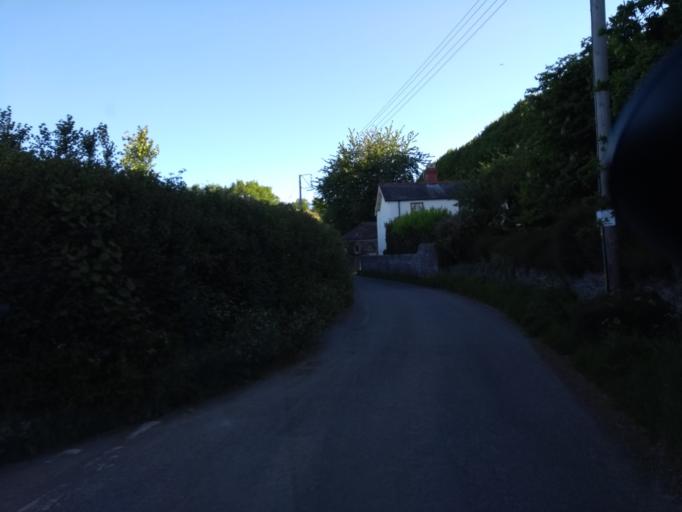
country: GB
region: England
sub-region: Somerset
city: Creech Saint Michael
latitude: 51.0470
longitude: -3.0560
